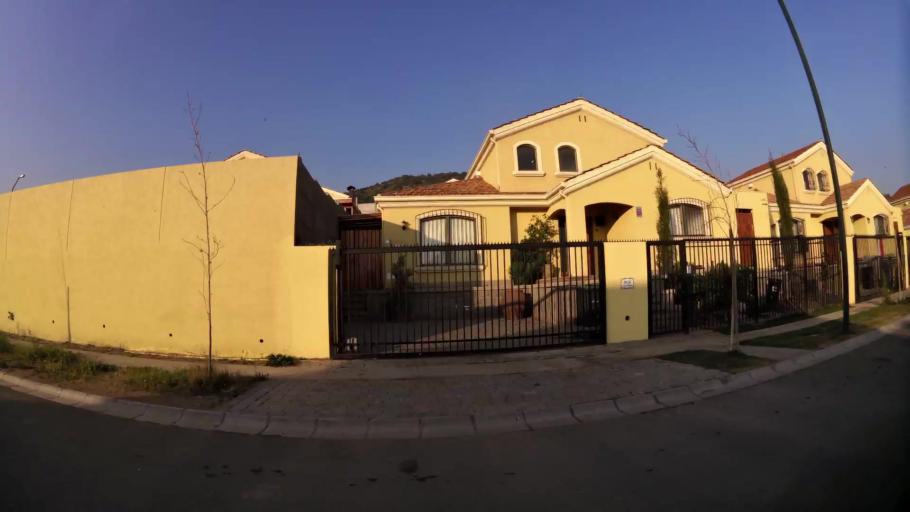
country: CL
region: Santiago Metropolitan
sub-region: Provincia de Santiago
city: Villa Presidente Frei, Nunoa, Santiago, Chile
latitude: -33.3289
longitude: -70.5024
